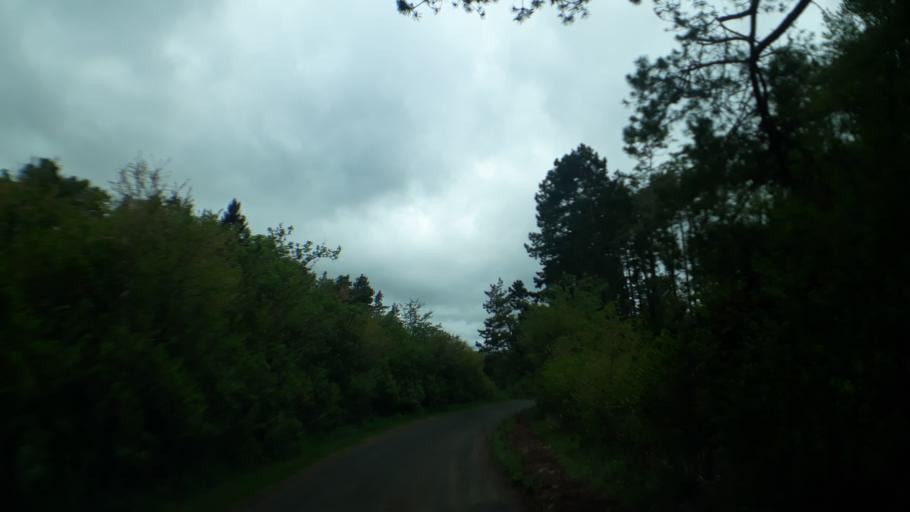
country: DE
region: North Rhine-Westphalia
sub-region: Regierungsbezirk Koln
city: Nettersheim
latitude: 50.5215
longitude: 6.6203
